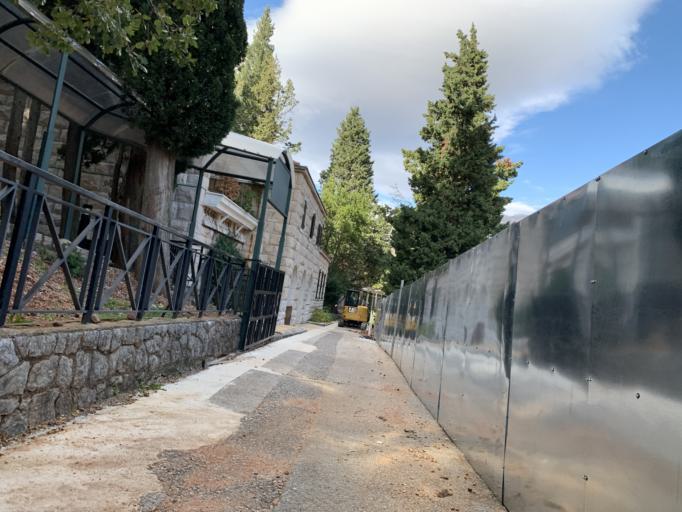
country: ME
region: Budva
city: Budva
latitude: 42.2654
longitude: 18.8921
